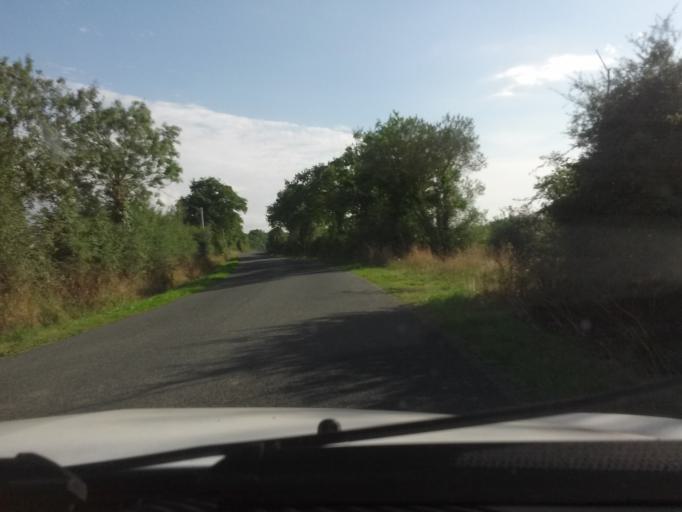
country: FR
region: Pays de la Loire
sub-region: Departement de la Loire-Atlantique
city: Saint-Hilaire-de-Clisson
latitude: 47.0265
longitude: -1.3031
